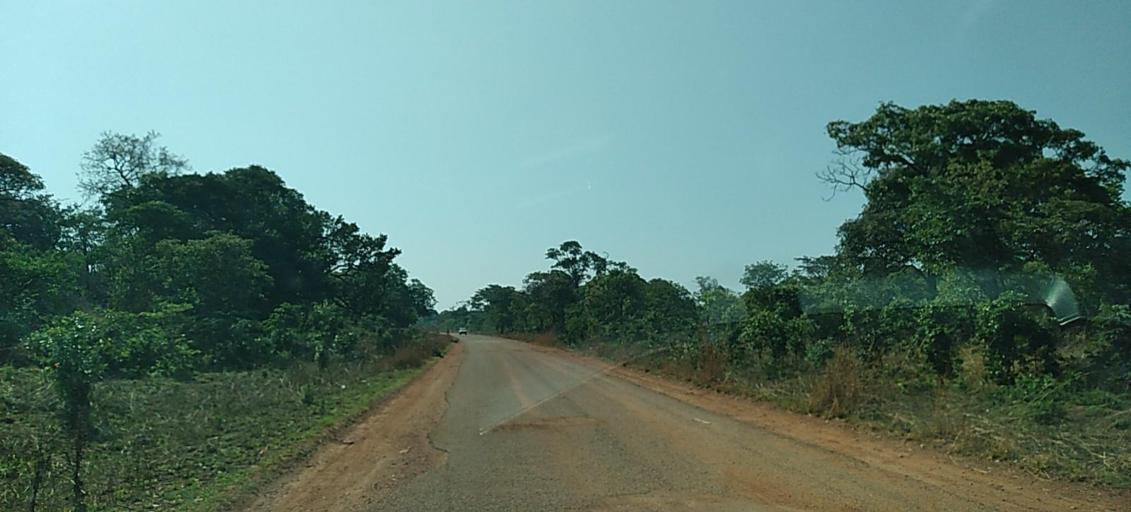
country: ZM
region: North-Western
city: Mwinilunga
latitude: -11.8996
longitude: 25.2769
